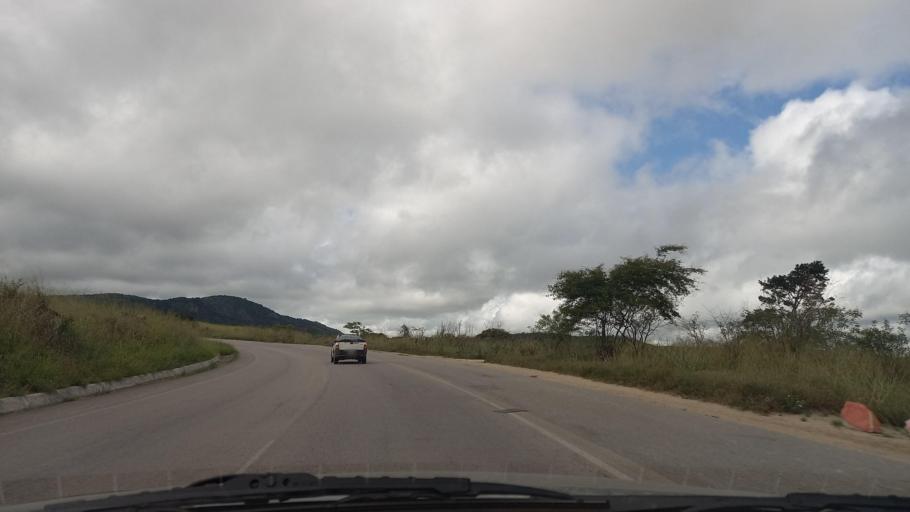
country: BR
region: Pernambuco
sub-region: Caruaru
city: Caruaru
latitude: -8.3206
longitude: -35.9913
